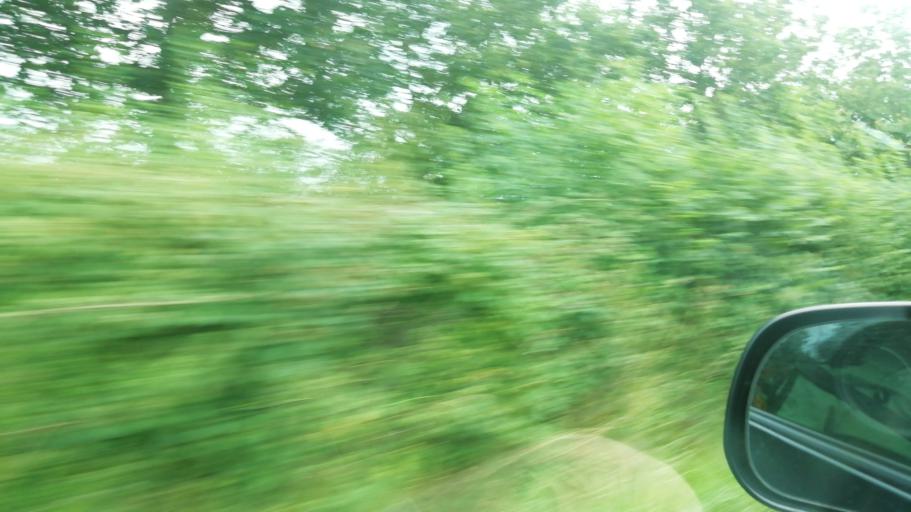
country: IE
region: Munster
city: Fethard
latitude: 52.4801
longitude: -7.6929
